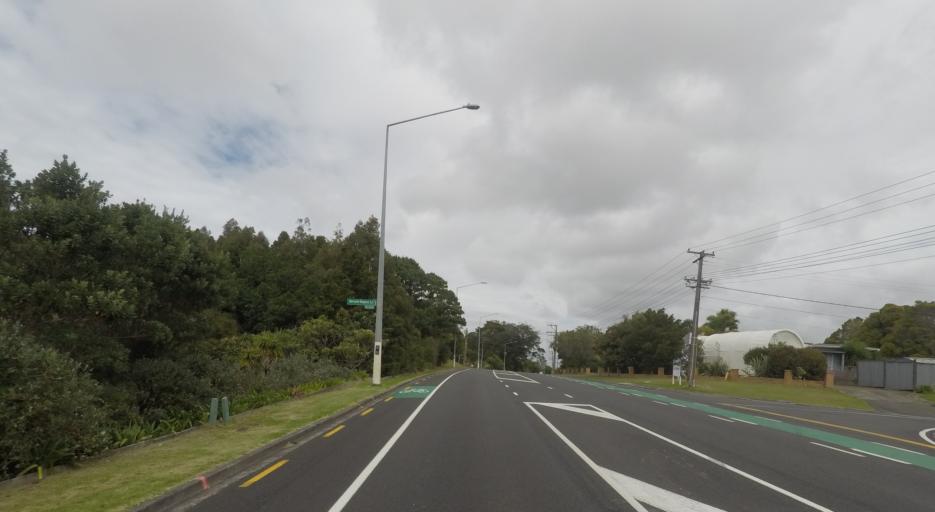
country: NZ
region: Auckland
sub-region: Auckland
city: North Shore
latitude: -36.7729
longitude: 174.6934
